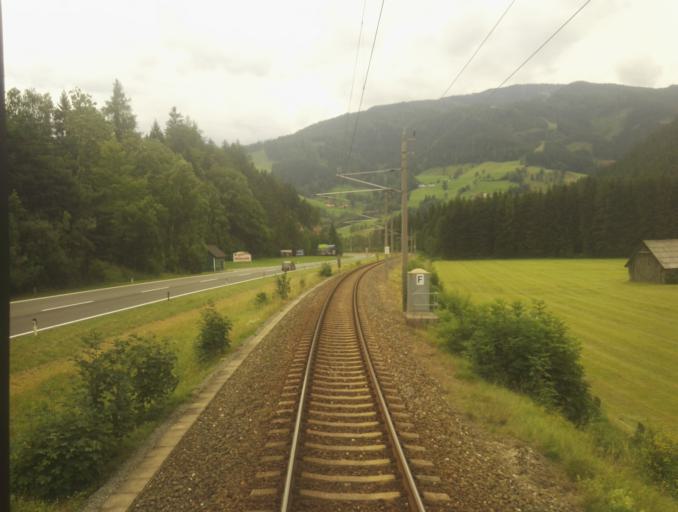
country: AT
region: Salzburg
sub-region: Politischer Bezirk Sankt Johann im Pongau
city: Forstau
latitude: 47.3958
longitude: 13.5910
